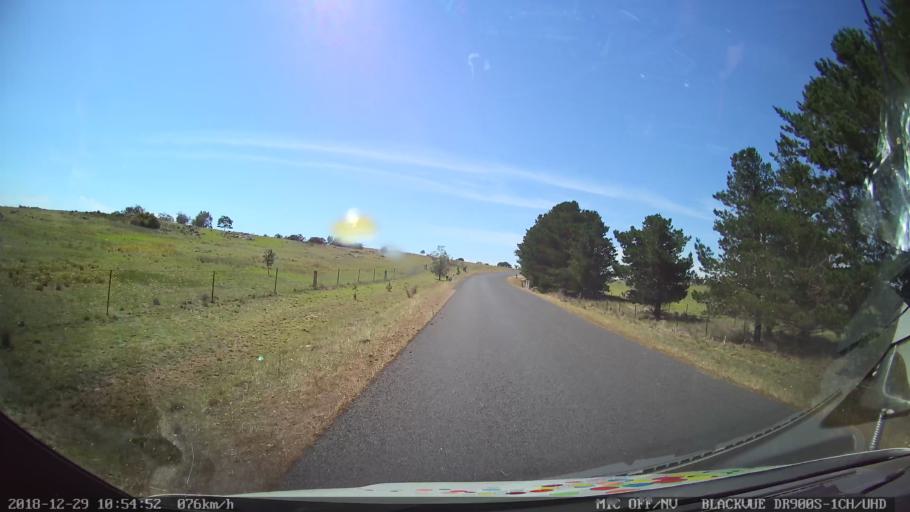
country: AU
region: New South Wales
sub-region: Palerang
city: Bungendore
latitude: -35.1186
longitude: 149.5300
